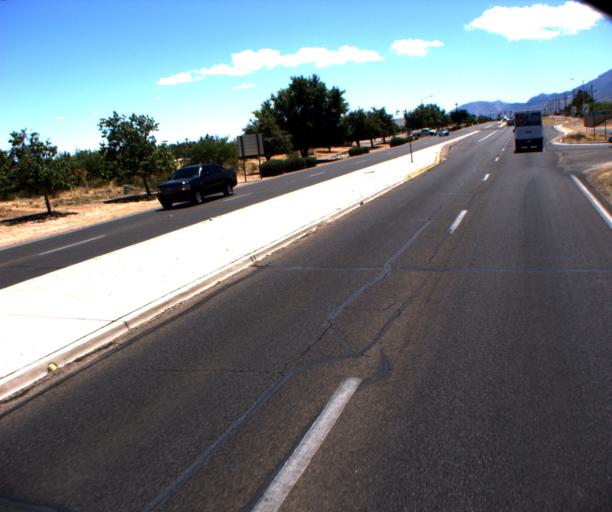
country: US
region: Arizona
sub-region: Cochise County
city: Sierra Vista
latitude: 31.5501
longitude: -110.2574
